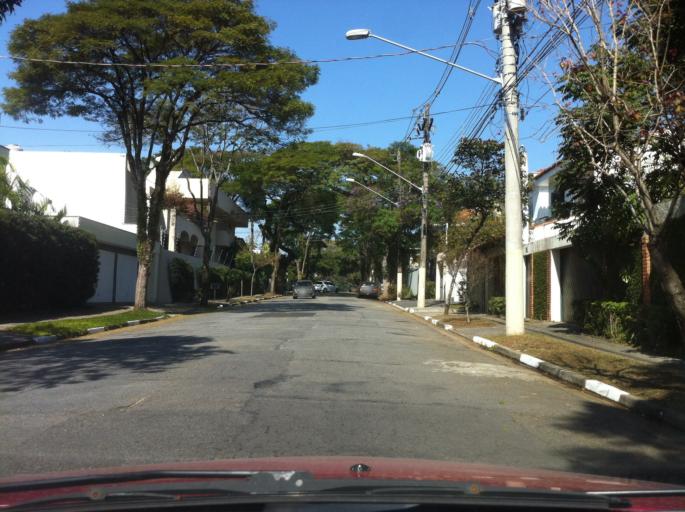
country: BR
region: Sao Paulo
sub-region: Sao Paulo
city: Sao Paulo
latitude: -23.6106
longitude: -46.6502
